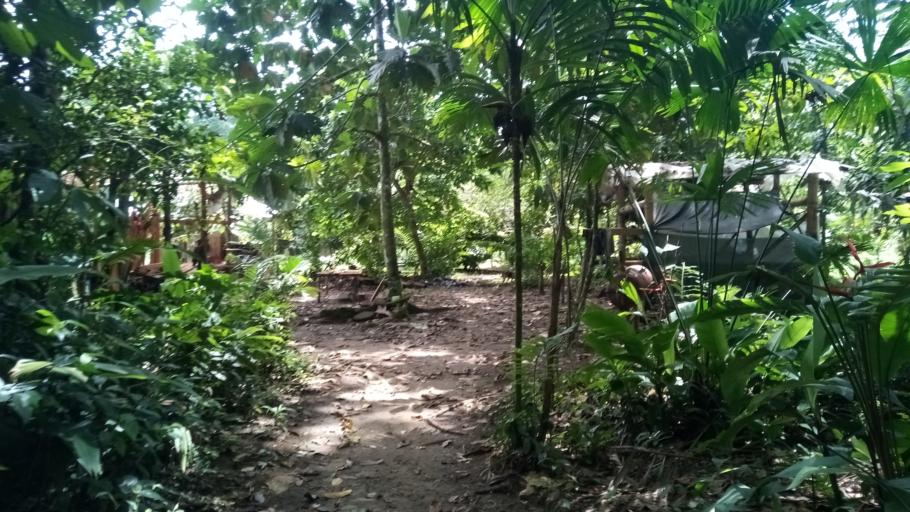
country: CR
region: Limon
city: Sixaola
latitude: 9.6234
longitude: -82.6210
